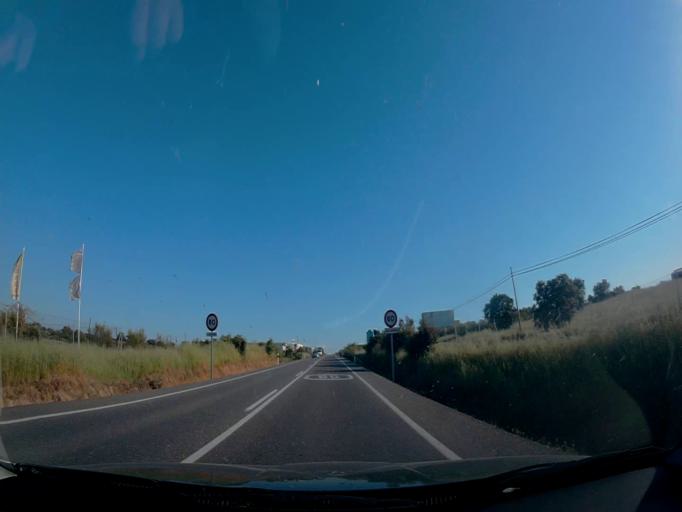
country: ES
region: Castille-La Mancha
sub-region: Province of Toledo
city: Escalona
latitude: 40.1359
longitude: -4.4043
